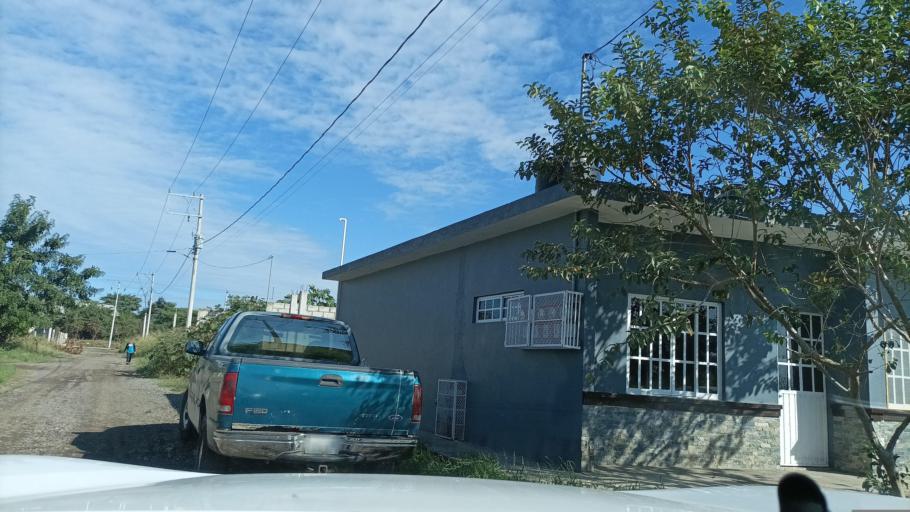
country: MX
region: Veracruz
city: Paso del Macho
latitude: 18.9712
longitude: -96.7140
